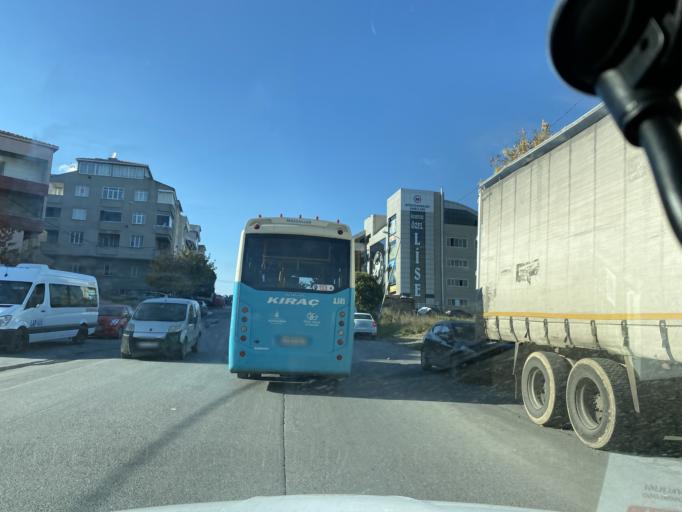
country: TR
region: Istanbul
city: Esenyurt
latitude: 41.0465
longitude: 28.6492
